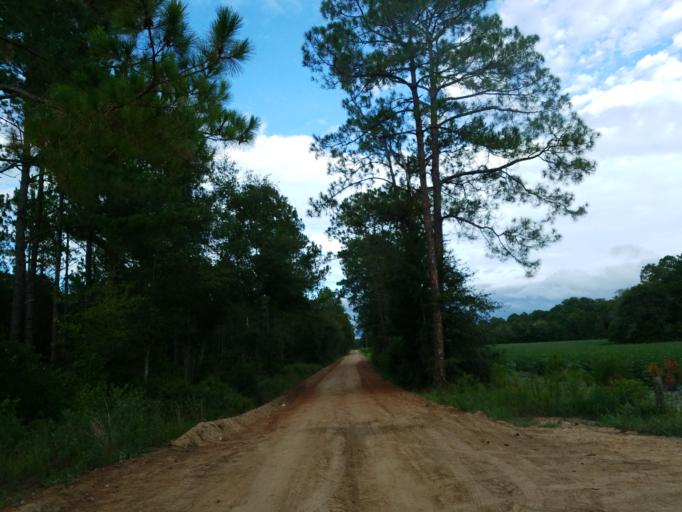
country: US
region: Georgia
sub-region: Cook County
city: Sparks
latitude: 31.2353
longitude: -83.4547
